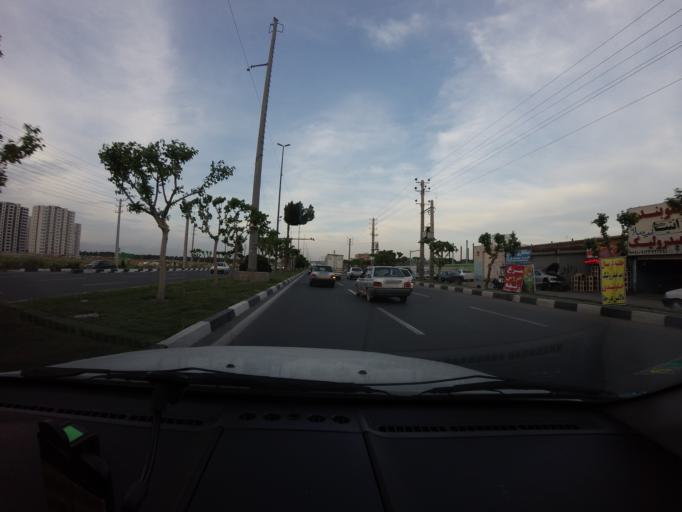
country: IR
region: Tehran
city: Eslamshahr
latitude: 35.5396
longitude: 51.2101
